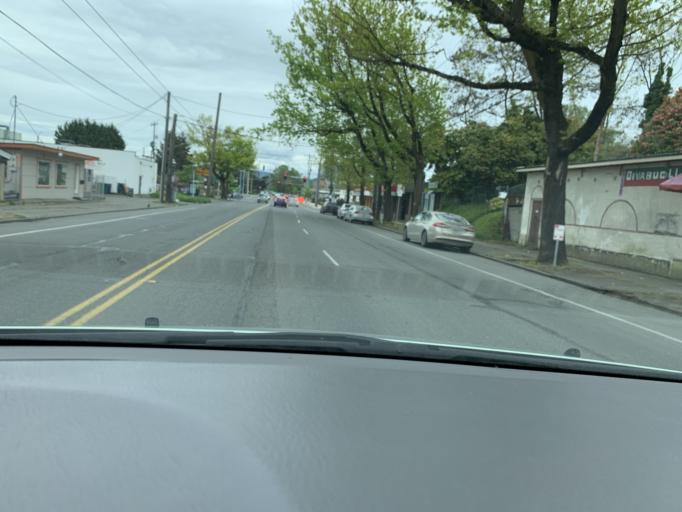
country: US
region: Washington
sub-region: King County
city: Bryn Mawr-Skyway
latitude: 47.5199
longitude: -122.2643
